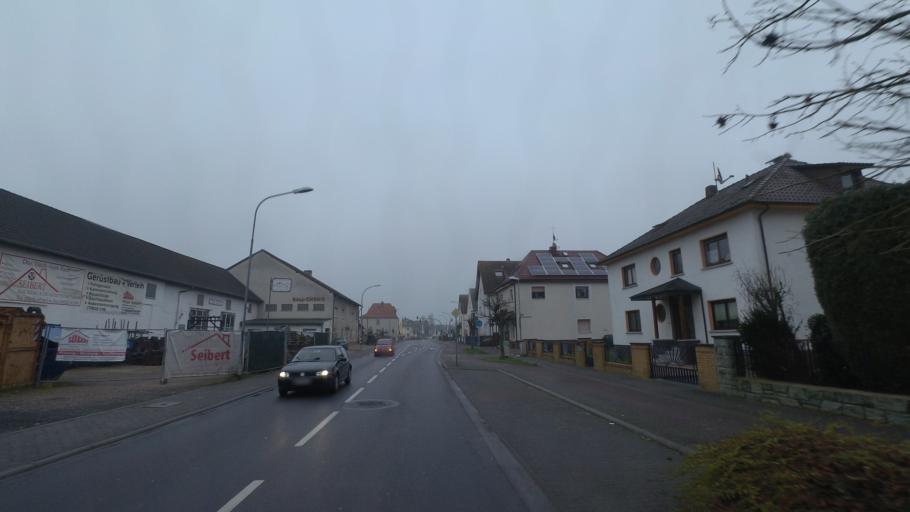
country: DE
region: Hesse
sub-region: Regierungsbezirk Darmstadt
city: Grosskrotzenburg
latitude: 50.0754
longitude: 8.9320
